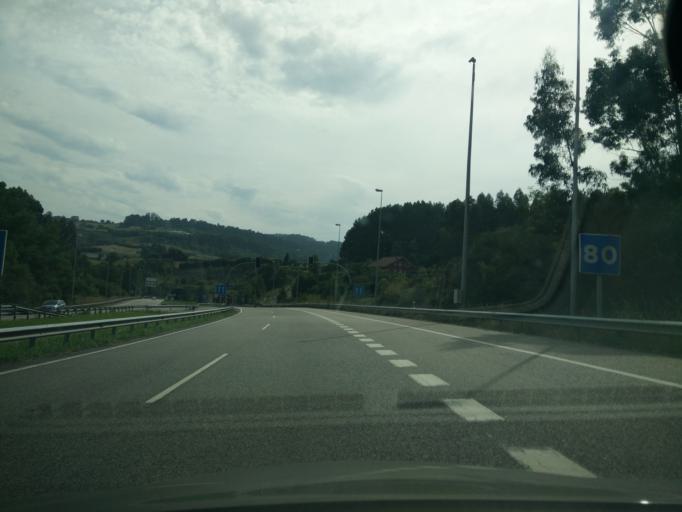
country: ES
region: Asturias
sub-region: Province of Asturias
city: Arriba
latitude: 43.5102
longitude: -5.5772
